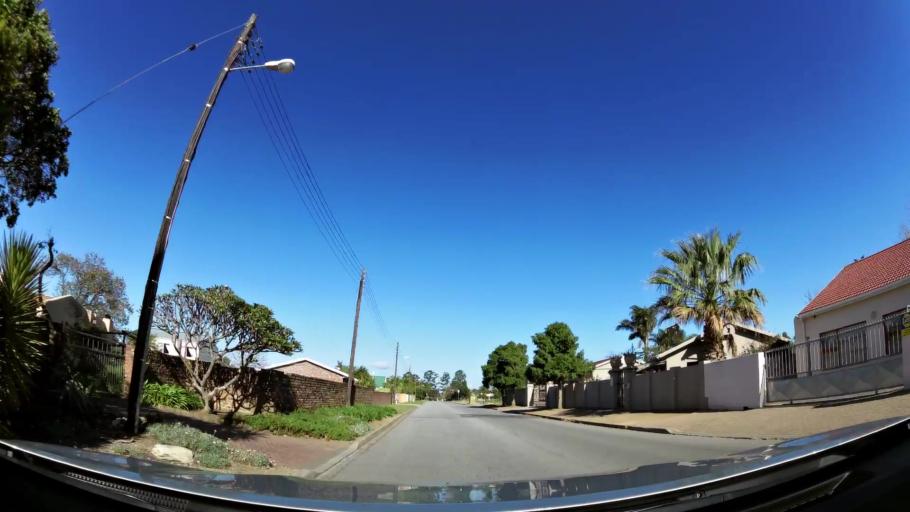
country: ZA
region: Western Cape
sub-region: Eden District Municipality
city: George
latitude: -33.9476
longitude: 22.4169
